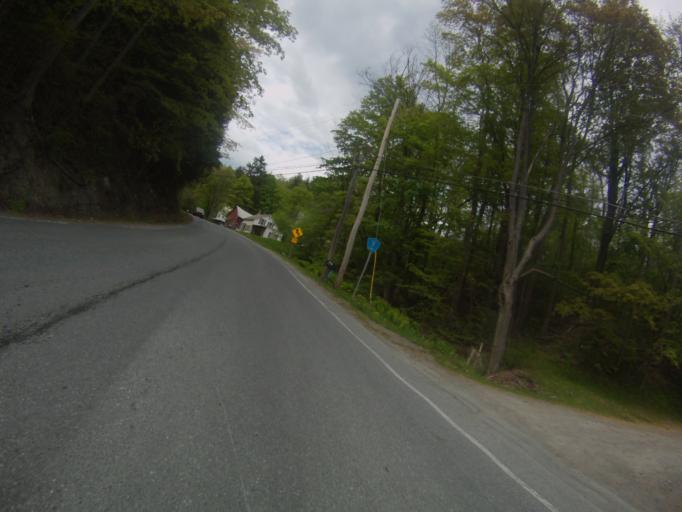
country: US
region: New York
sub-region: Essex County
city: Ticonderoga
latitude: 43.9422
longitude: -73.4693
